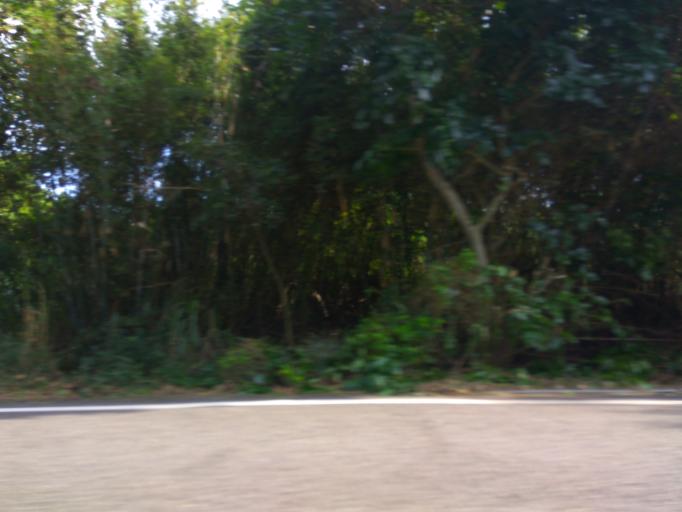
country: TW
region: Taiwan
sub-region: Hsinchu
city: Zhubei
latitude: 24.9494
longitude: 120.9951
